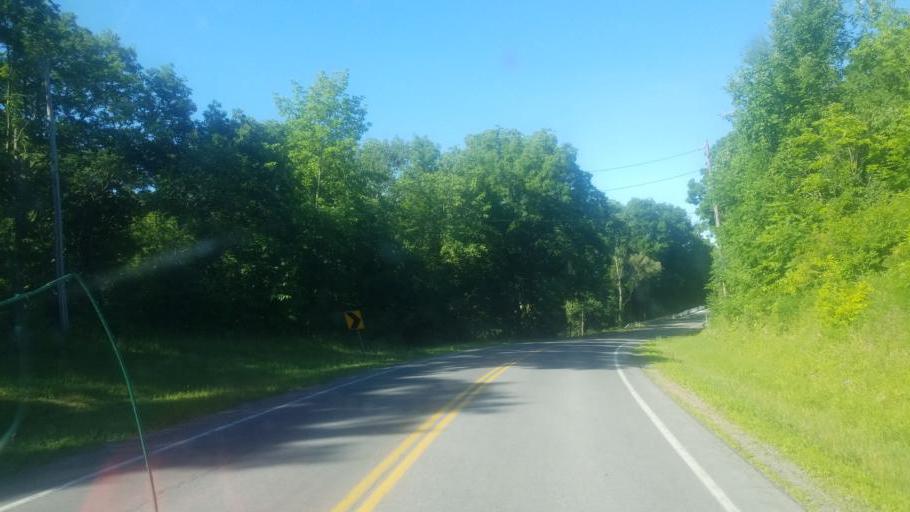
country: US
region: New York
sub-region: Ontario County
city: Clifton Springs
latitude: 42.8443
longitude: -77.1091
